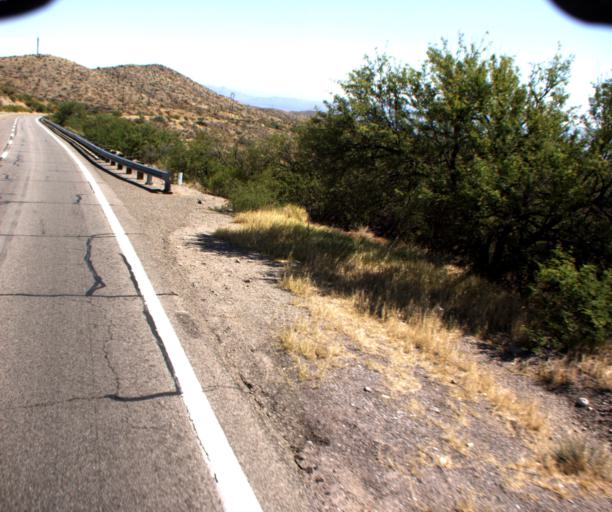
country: US
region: Arizona
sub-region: Pinal County
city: Oracle
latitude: 32.6407
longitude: -110.7236
